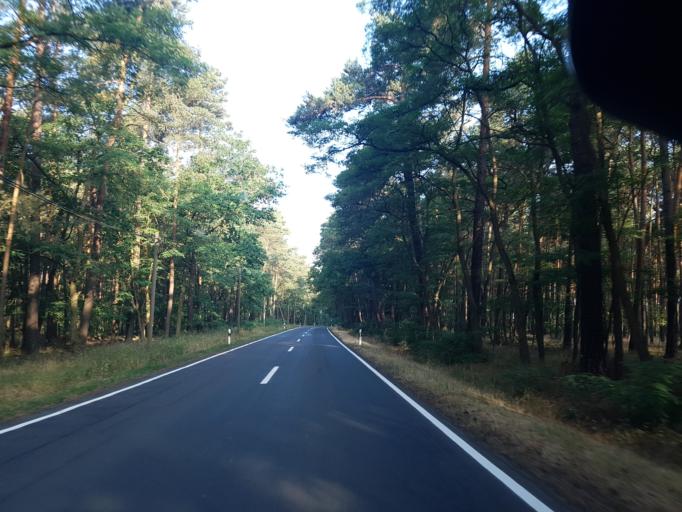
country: DE
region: Brandenburg
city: Ihlow
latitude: 51.8117
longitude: 13.2540
